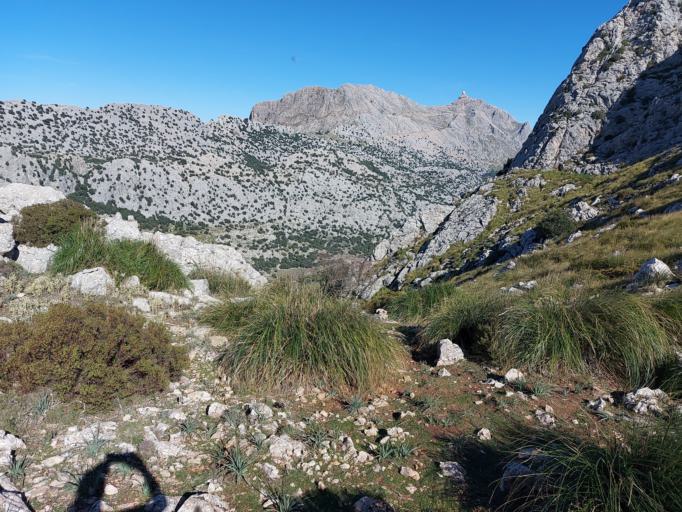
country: ES
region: Balearic Islands
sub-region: Illes Balears
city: Fornalutx
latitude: 39.7708
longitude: 2.7786
